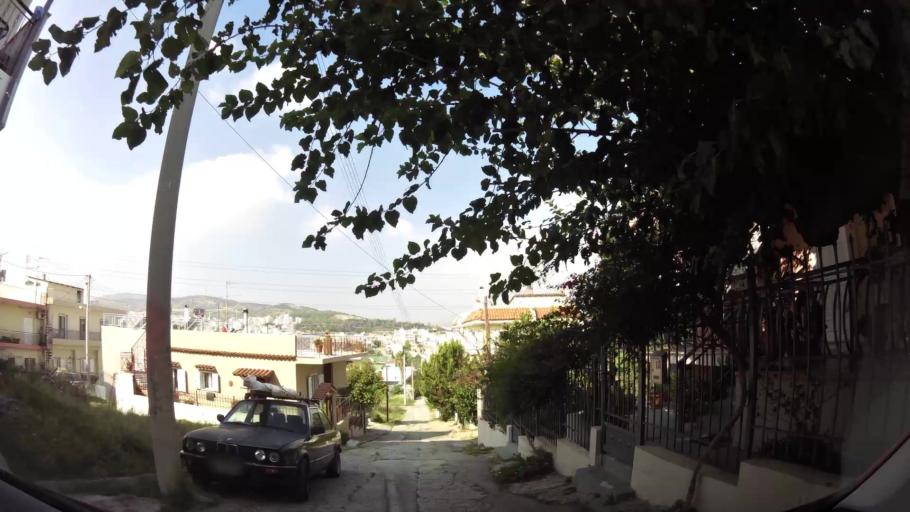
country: GR
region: Attica
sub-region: Nomarchia Dytikis Attikis
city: Zefyri
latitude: 38.0619
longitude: 23.7228
